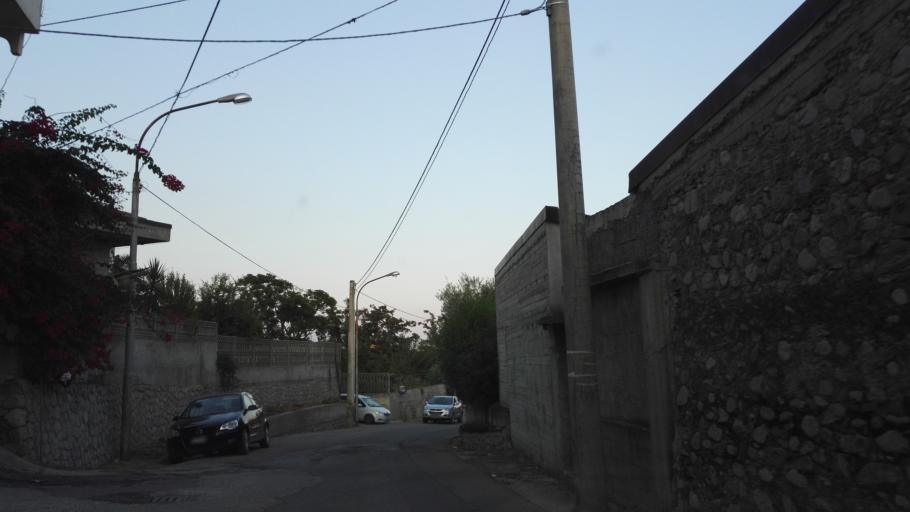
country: IT
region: Calabria
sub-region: Provincia di Reggio Calabria
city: Caulonia Marina
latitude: 38.3618
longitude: 16.4681
